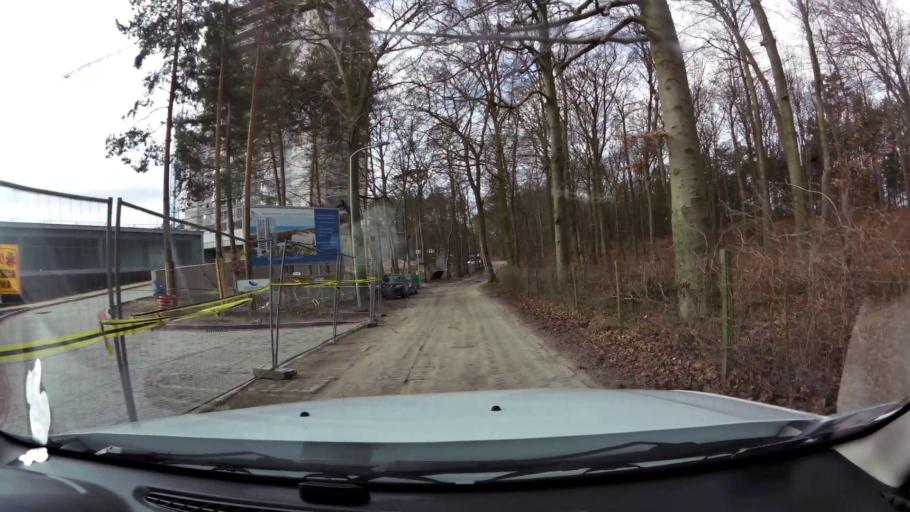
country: PL
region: West Pomeranian Voivodeship
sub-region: Powiat kamienski
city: Miedzyzdroje
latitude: 53.9235
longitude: 14.4264
